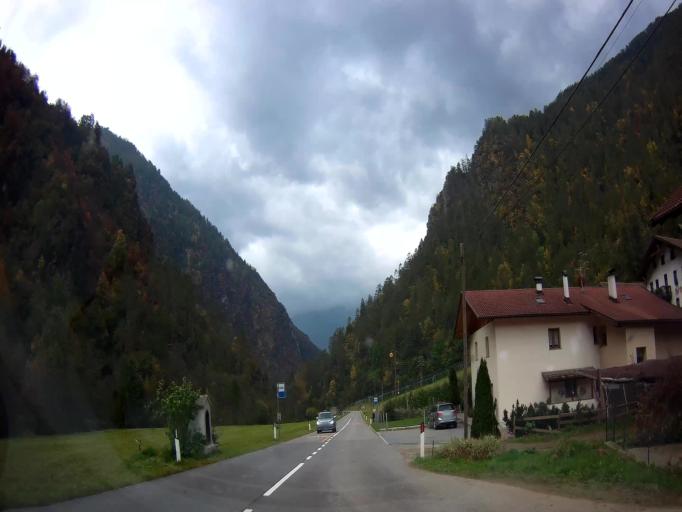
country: IT
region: Trentino-Alto Adige
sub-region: Bolzano
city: Certosa
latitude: 46.6720
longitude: 10.9434
